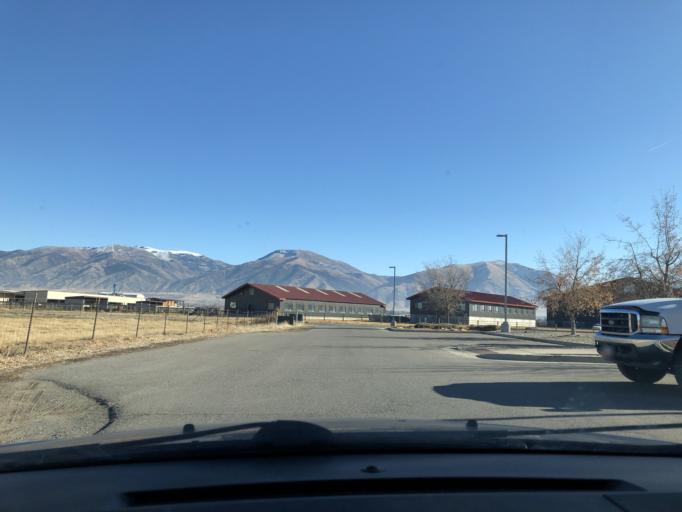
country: US
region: Utah
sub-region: Cache County
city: Wellsville
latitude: 41.6656
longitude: -111.8917
